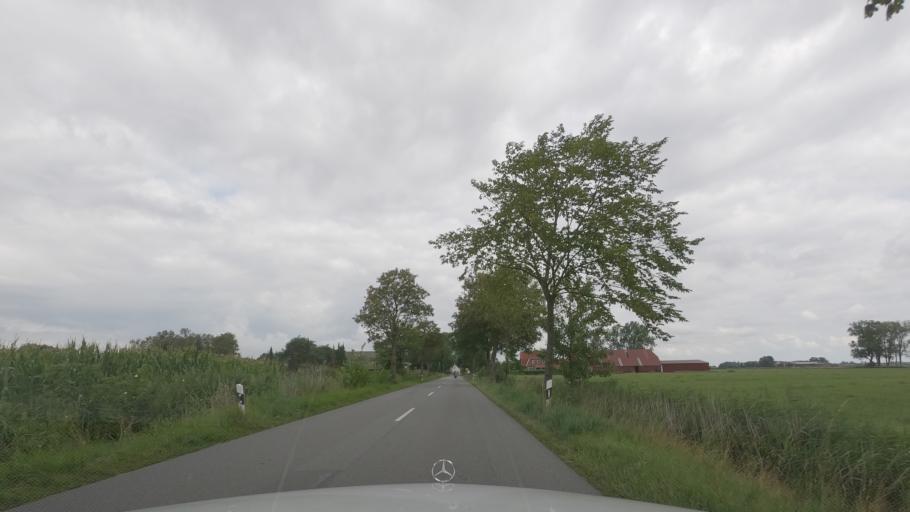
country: DE
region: Lower Saxony
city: Uthlede
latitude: 53.2922
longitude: 8.5307
